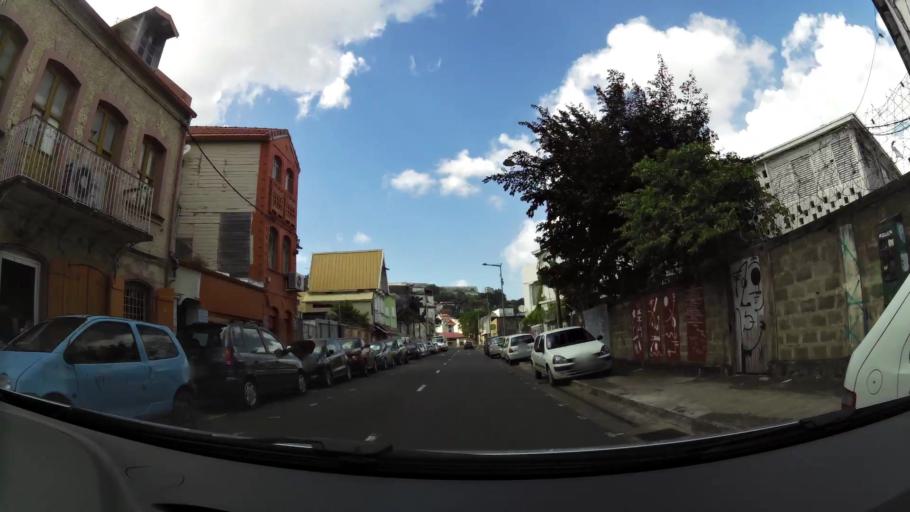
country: MQ
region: Martinique
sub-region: Martinique
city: Fort-de-France
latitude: 14.6070
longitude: -61.0714
